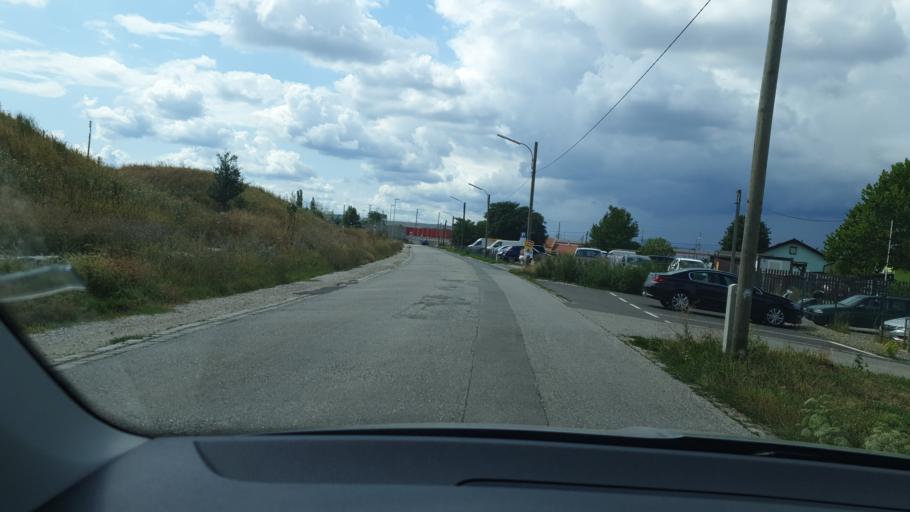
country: AT
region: Lower Austria
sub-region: Politischer Bezirk Modling
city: Hennersdorf
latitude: 48.1386
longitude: 16.3734
